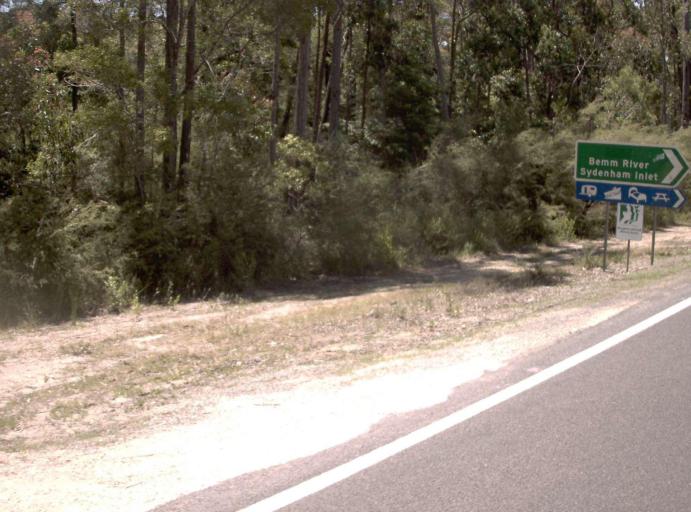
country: AU
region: Victoria
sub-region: East Gippsland
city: Lakes Entrance
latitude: -37.6727
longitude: 148.7937
